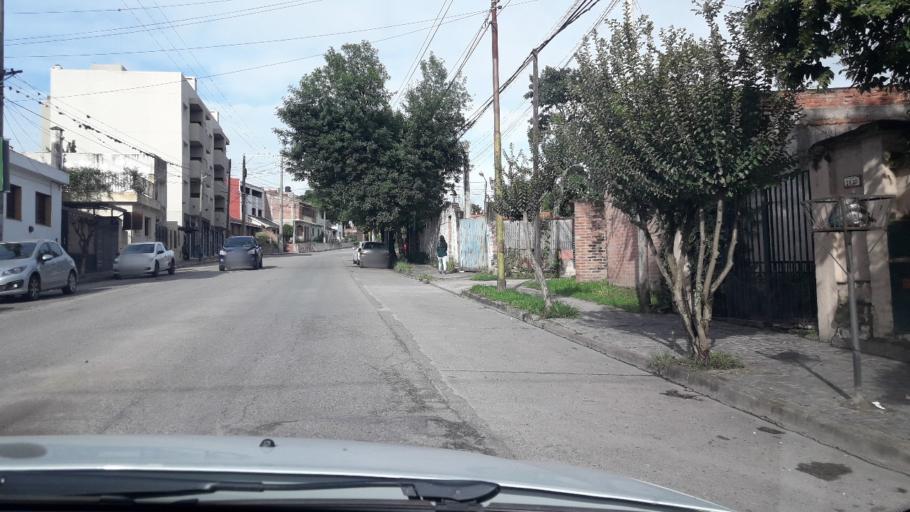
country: AR
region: Jujuy
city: San Salvador de Jujuy
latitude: -24.1793
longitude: -65.3346
